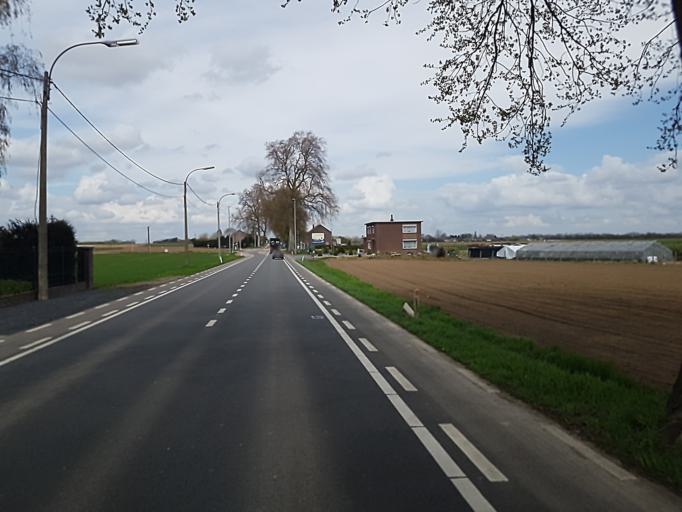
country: BE
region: Flanders
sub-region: Provincie Limburg
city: Riemst
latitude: 50.8267
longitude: 5.6257
